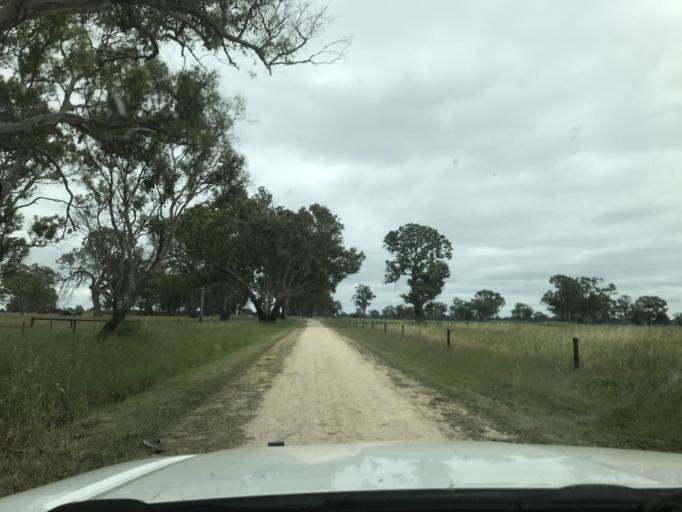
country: AU
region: South Australia
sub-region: Wattle Range
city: Penola
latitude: -37.1796
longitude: 141.0649
